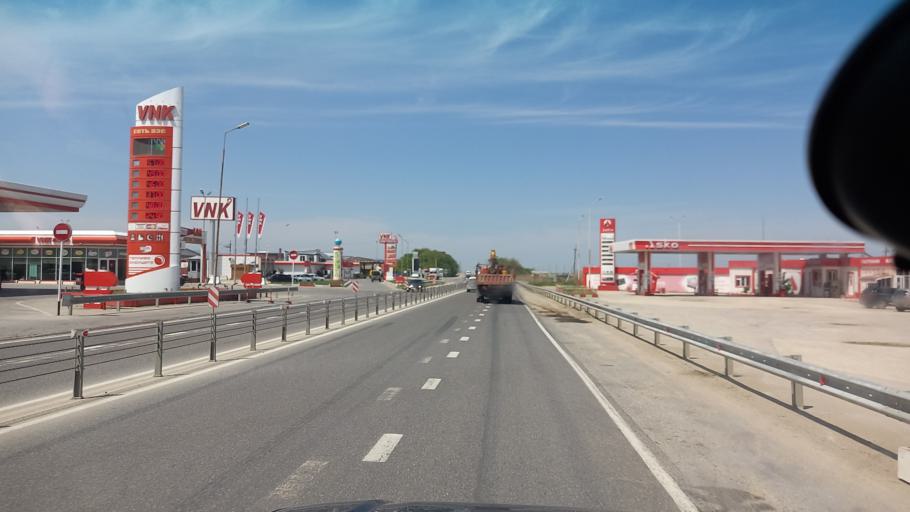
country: RU
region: Dagestan
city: Manas
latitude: 42.7236
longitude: 47.6681
